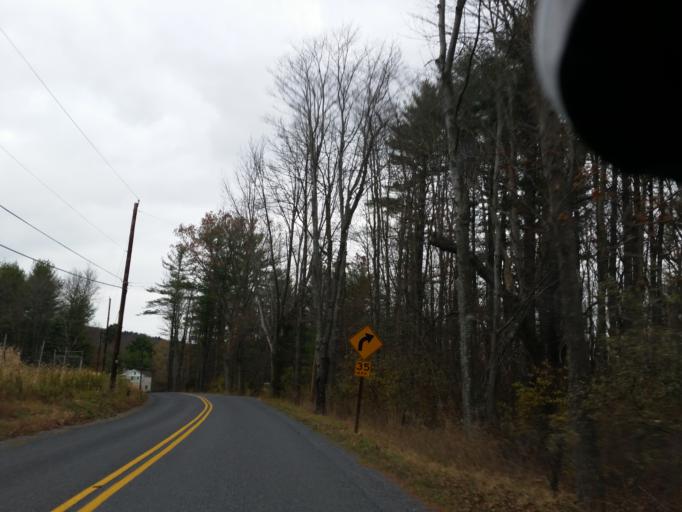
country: US
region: Pennsylvania
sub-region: Union County
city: New Columbia
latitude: 41.0454
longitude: -76.9477
